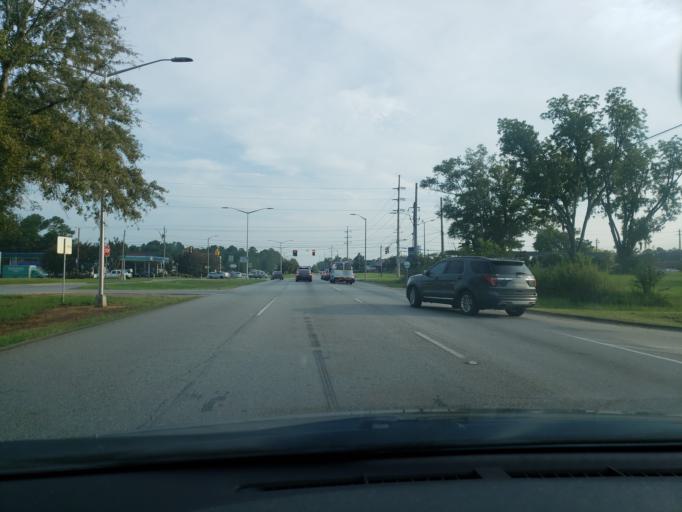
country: US
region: Georgia
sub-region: Dougherty County
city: Albany
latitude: 31.5848
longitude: -84.2193
